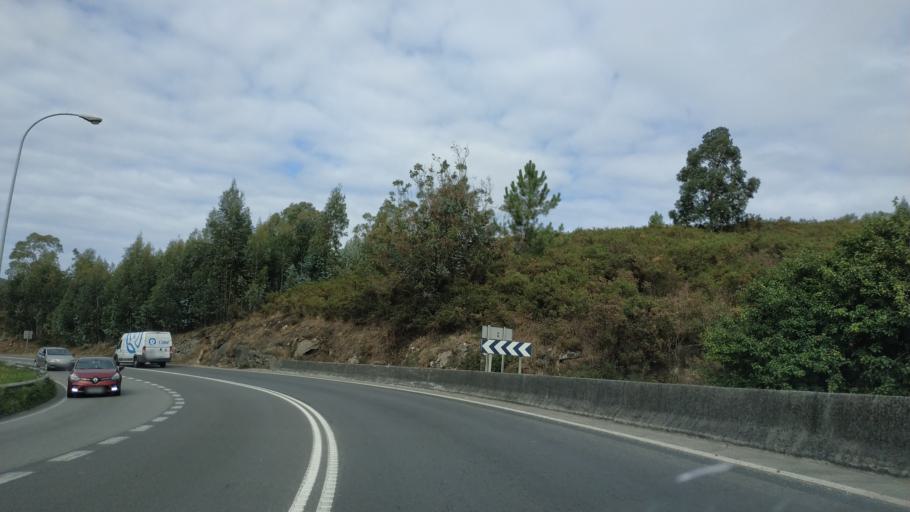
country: ES
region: Galicia
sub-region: Provincia da Coruna
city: Arteixo
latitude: 43.3342
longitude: -8.4526
